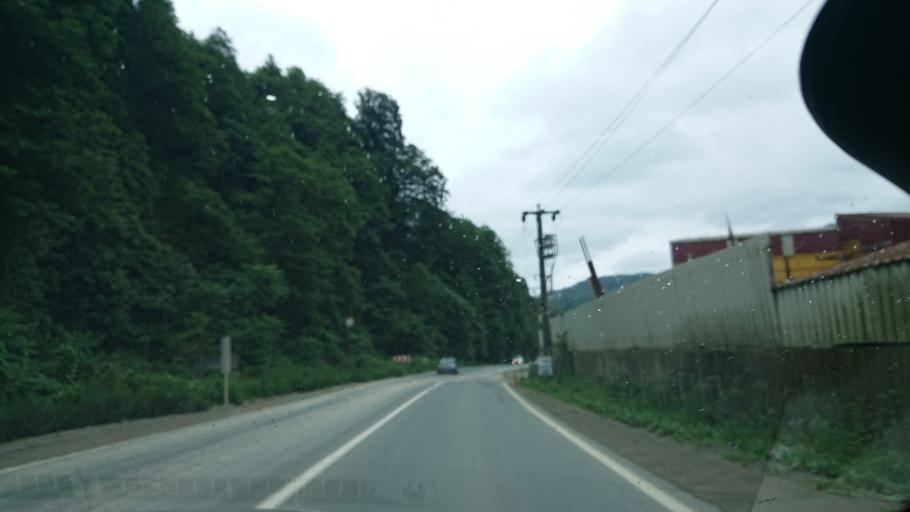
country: TR
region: Rize
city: Gundogdu
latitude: 41.0163
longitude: 40.5687
